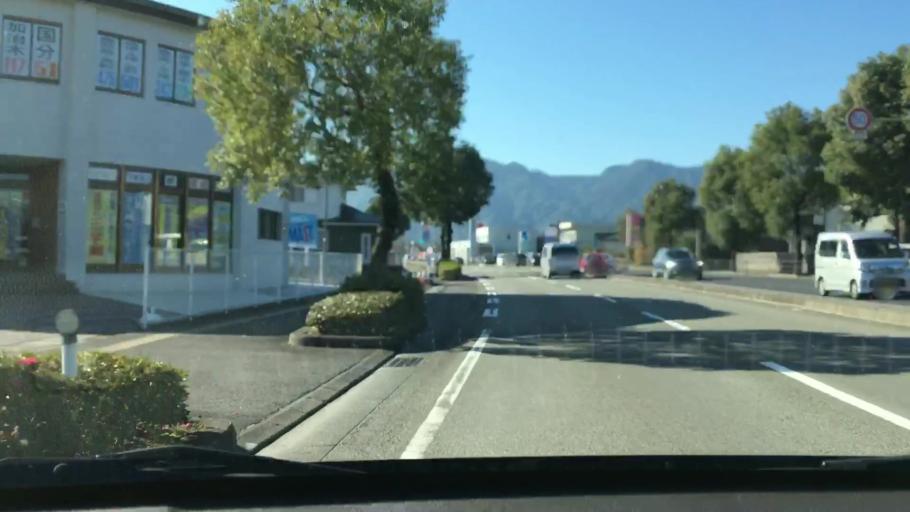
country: JP
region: Kagoshima
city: Kajiki
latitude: 31.7281
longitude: 130.6253
